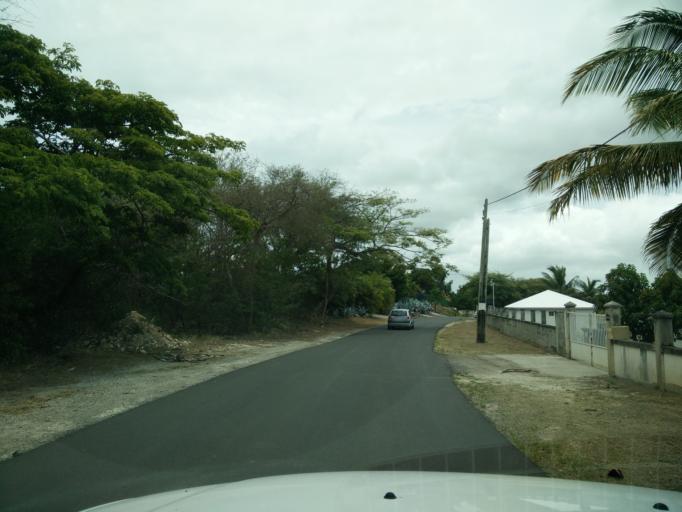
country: GP
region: Guadeloupe
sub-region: Guadeloupe
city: Sainte-Anne
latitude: 16.2460
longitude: -61.3553
